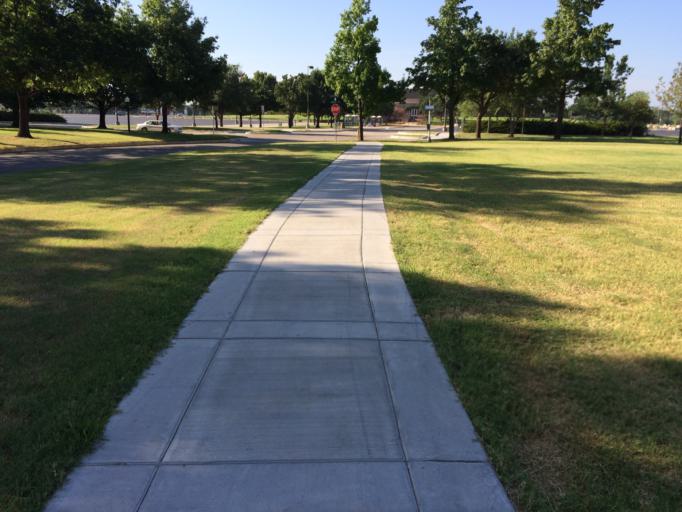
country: US
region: Oklahoma
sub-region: Cleveland County
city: Norman
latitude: 35.1902
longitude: -97.4447
